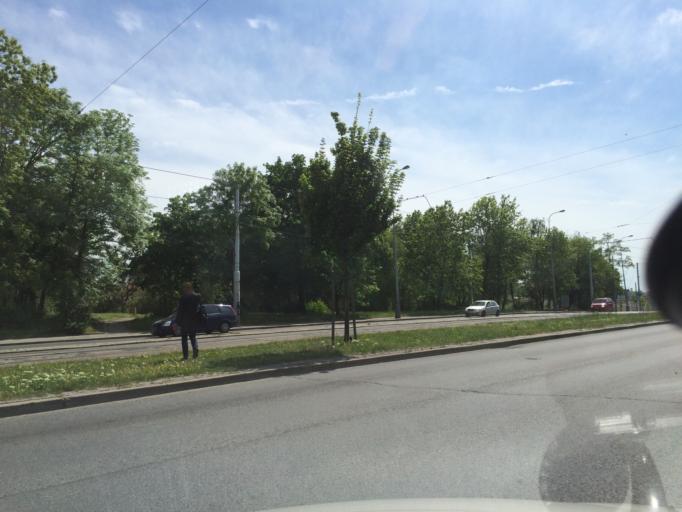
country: CZ
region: Praha
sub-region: Praha 1
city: Mala Strana
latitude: 50.0937
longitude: 14.3890
